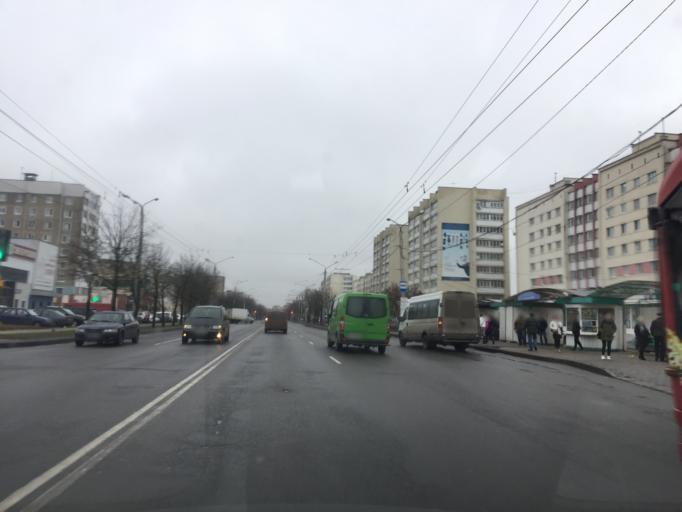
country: BY
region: Mogilev
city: Mahilyow
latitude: 53.8707
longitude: 30.3488
